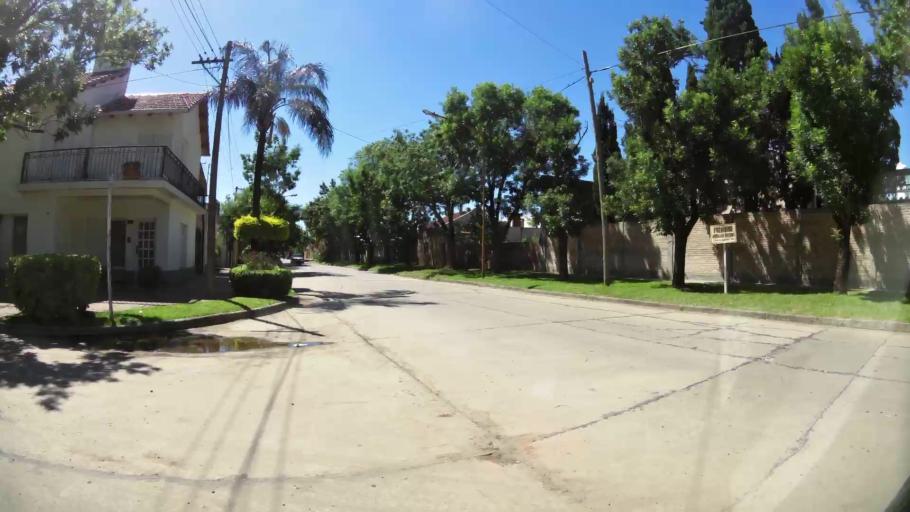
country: AR
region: Santa Fe
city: Esperanza
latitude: -31.4397
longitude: -60.9305
